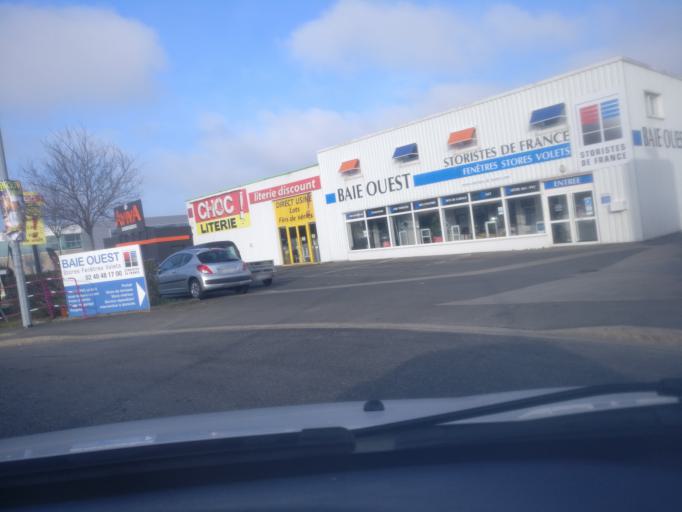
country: FR
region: Pays de la Loire
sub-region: Departement de la Loire-Atlantique
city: Vertou
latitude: 47.1871
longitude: -1.4632
